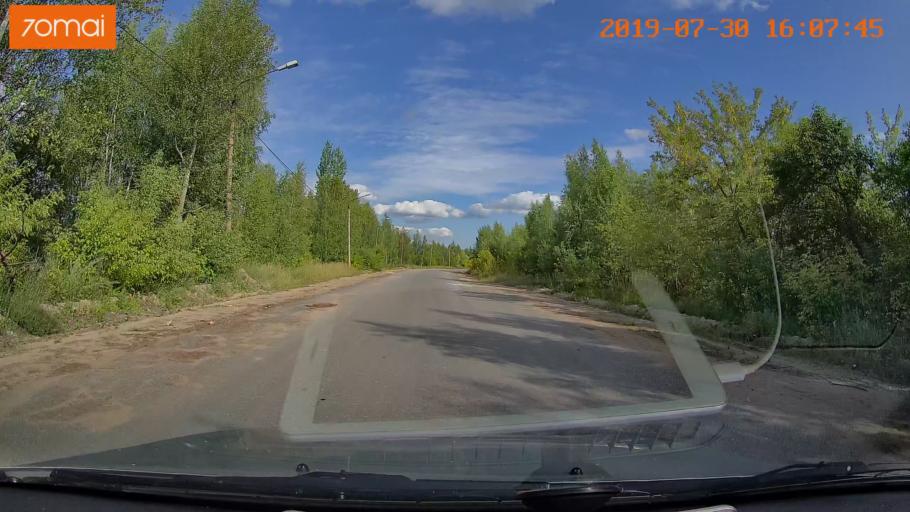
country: RU
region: Moskovskaya
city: Peski
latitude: 55.2485
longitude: 38.7223
